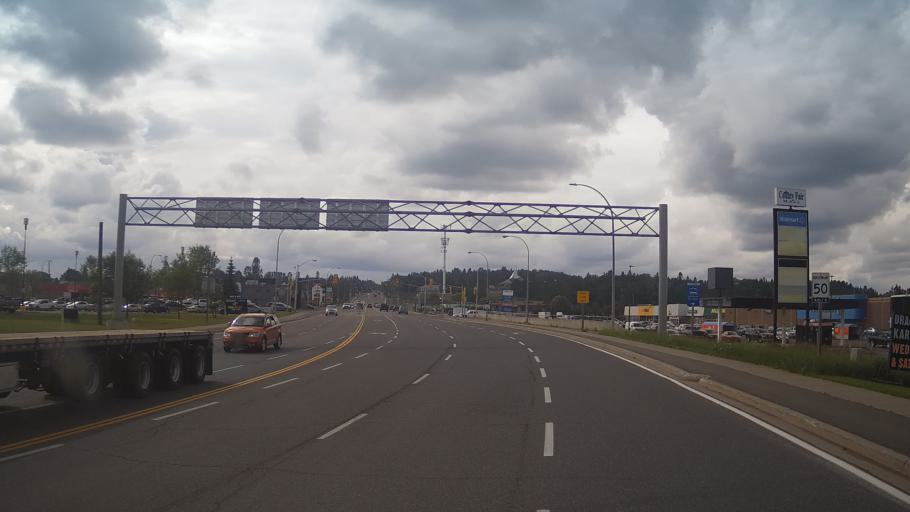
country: CA
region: Ontario
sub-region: Thunder Bay District
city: Thunder Bay
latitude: 48.4509
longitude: -89.2518
